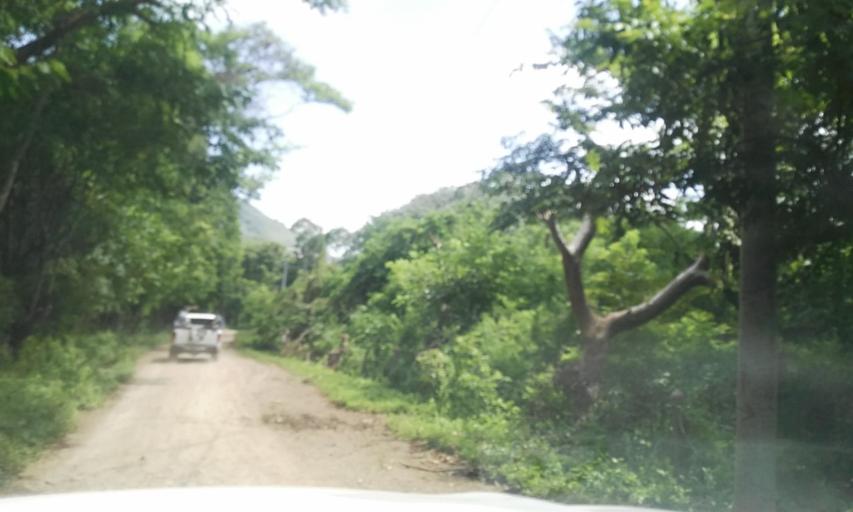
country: NI
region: Matagalpa
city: Terrabona
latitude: 12.7018
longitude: -85.9272
